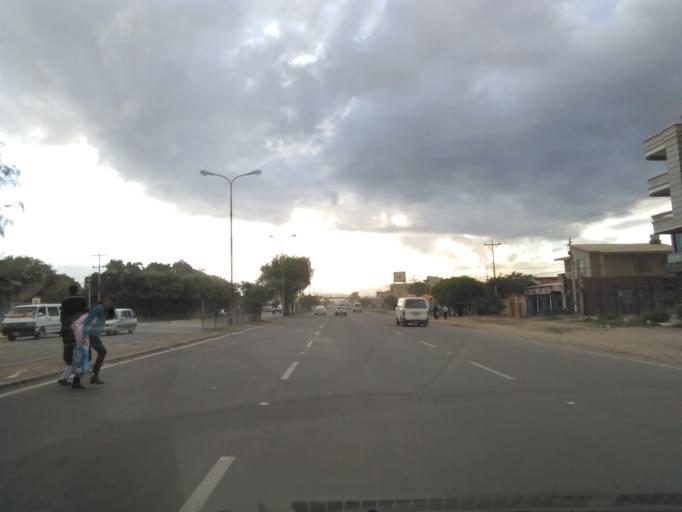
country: BO
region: Cochabamba
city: Cochabamba
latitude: -17.3915
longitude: -66.2248
